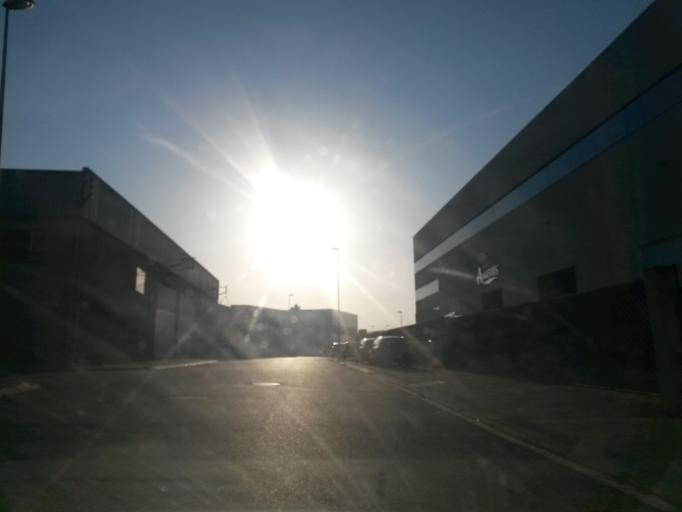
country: ES
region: Catalonia
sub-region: Provincia de Girona
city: Fornells de la Selva
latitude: 41.9330
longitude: 2.7985
